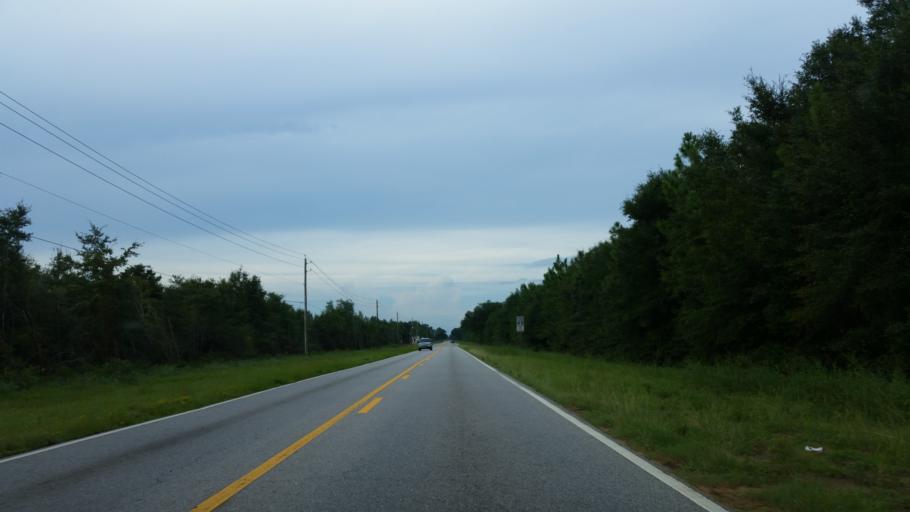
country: US
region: Florida
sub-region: Santa Rosa County
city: Pace
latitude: 30.5748
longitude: -87.1119
